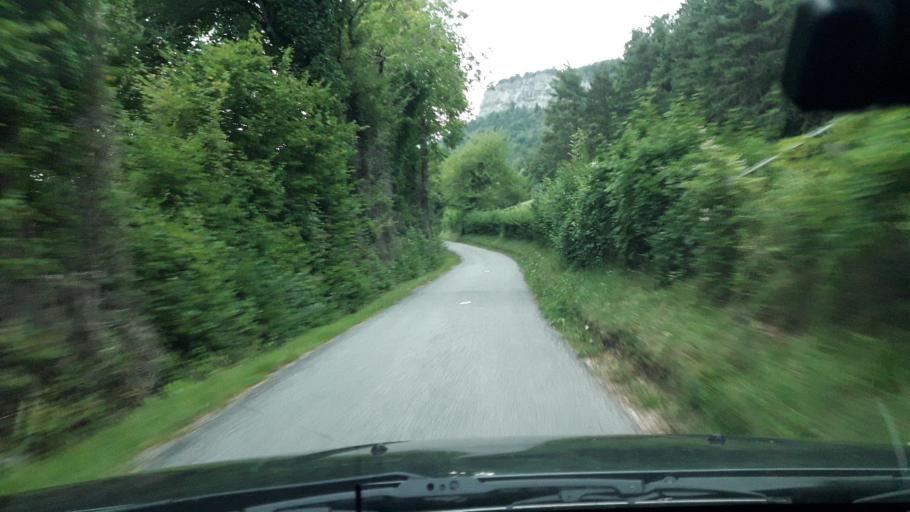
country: FR
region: Rhone-Alpes
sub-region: Departement de la Savoie
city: Barberaz
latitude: 45.5270
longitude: 5.9260
